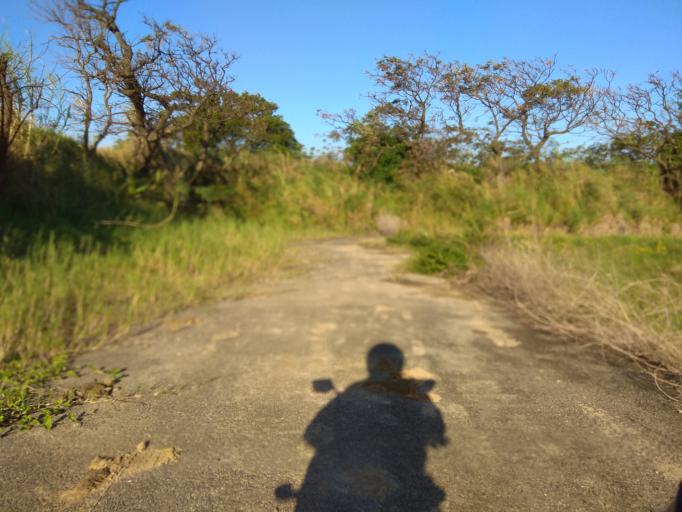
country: TW
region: Taiwan
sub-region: Hsinchu
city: Zhubei
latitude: 24.9961
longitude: 121.0533
